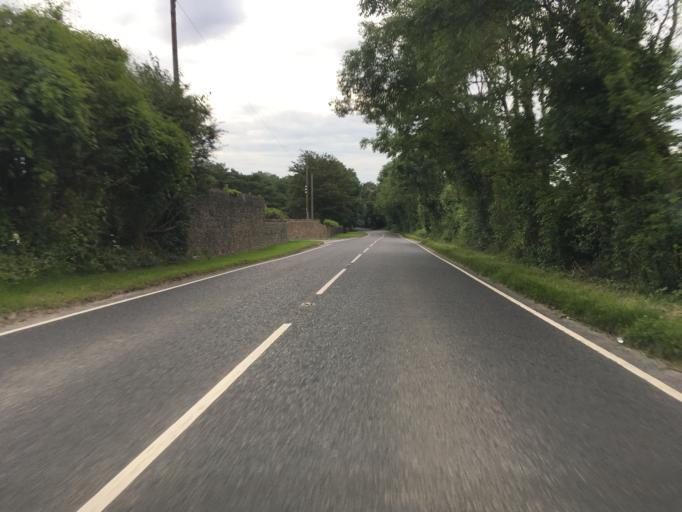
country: GB
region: England
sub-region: North Somerset
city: Long Ashton
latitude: 51.4439
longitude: -2.6731
